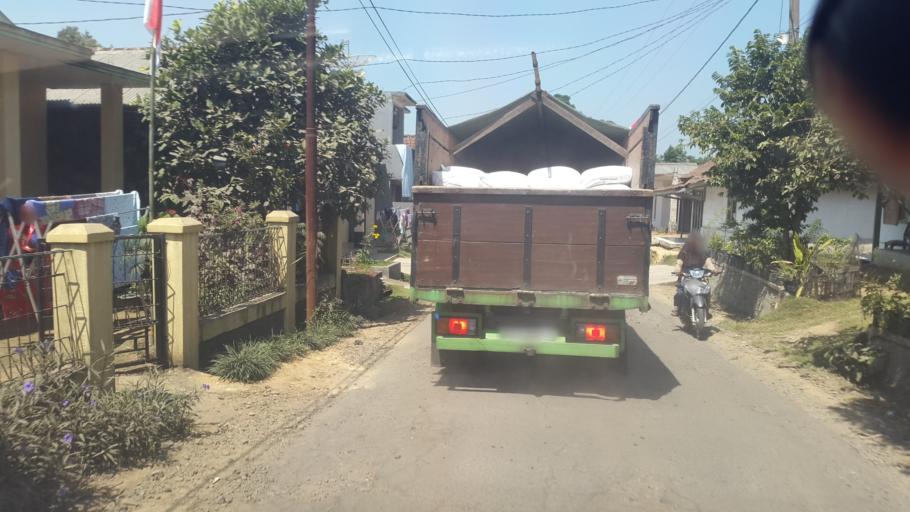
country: ID
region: Banten
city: Kubang
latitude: -6.7928
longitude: 106.6193
